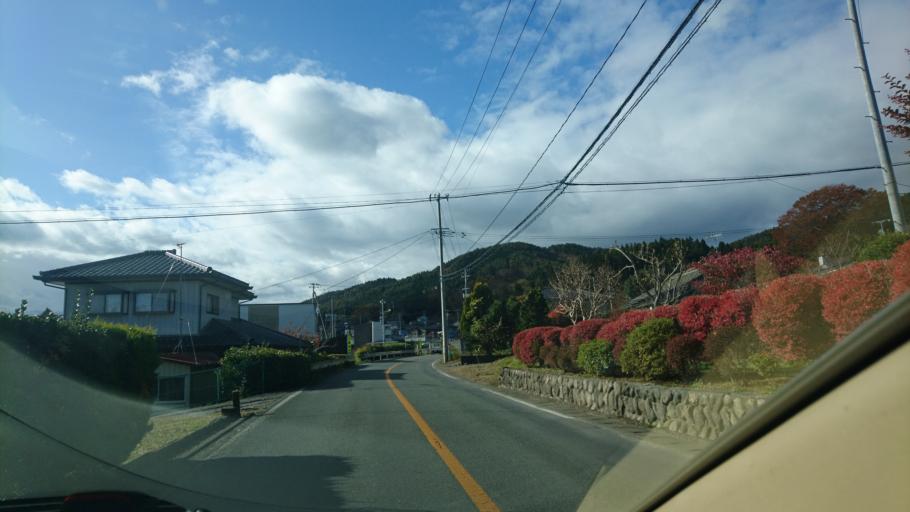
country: JP
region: Iwate
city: Ofunato
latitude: 39.0087
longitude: 141.7121
